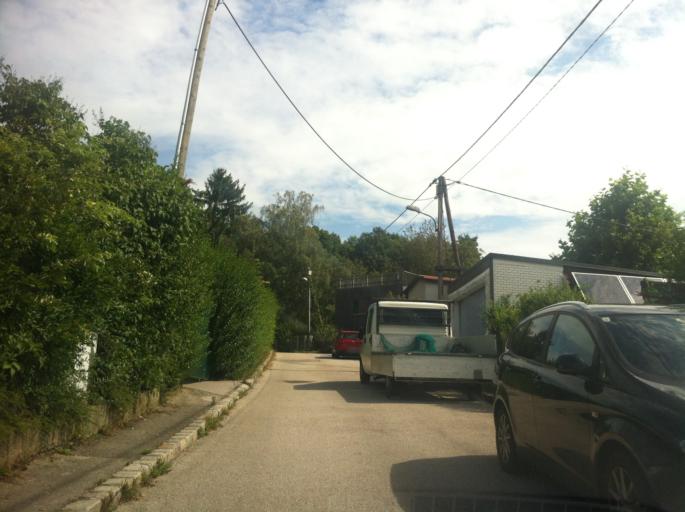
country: AT
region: Lower Austria
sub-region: Politischer Bezirk Wien-Umgebung
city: Gablitz
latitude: 48.2278
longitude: 16.1646
